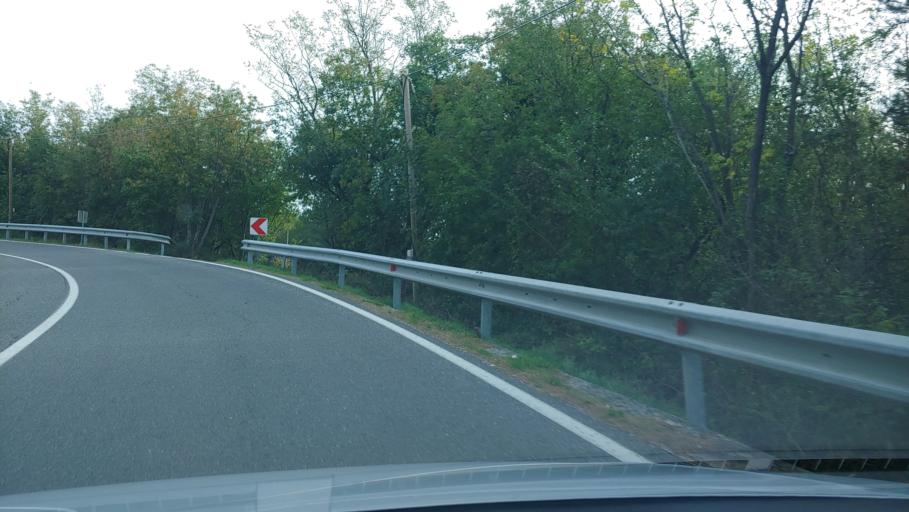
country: SI
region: Nova Gorica
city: Sempas
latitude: 45.9100
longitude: 13.7676
